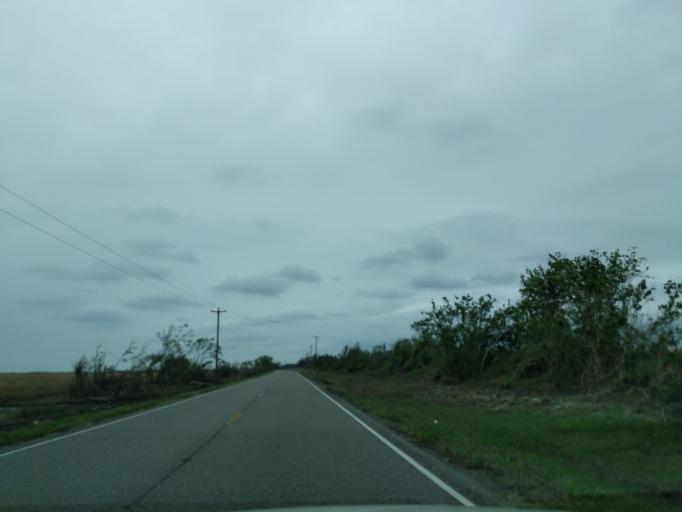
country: US
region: Louisiana
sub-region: Cameron Parish
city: Cameron
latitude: 29.7864
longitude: -93.1713
